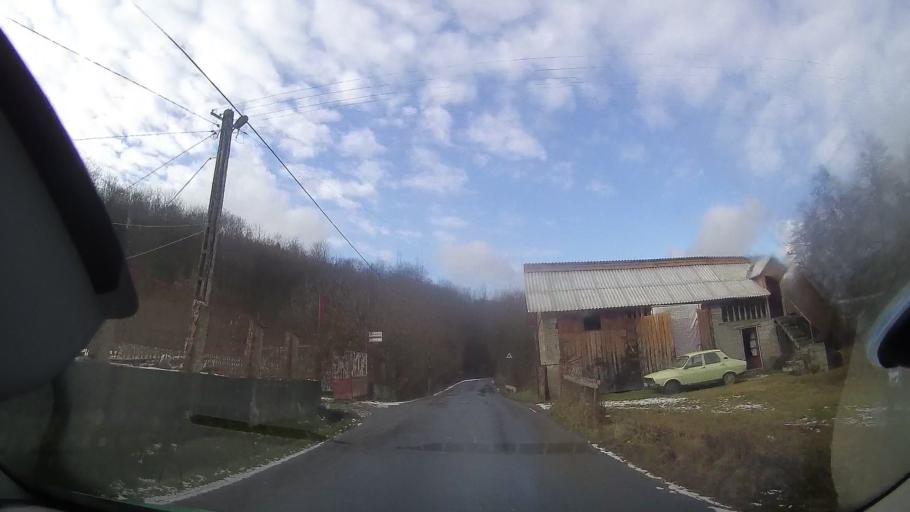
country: RO
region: Alba
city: Salciua de Sus
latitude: 46.4261
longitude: 23.4518
